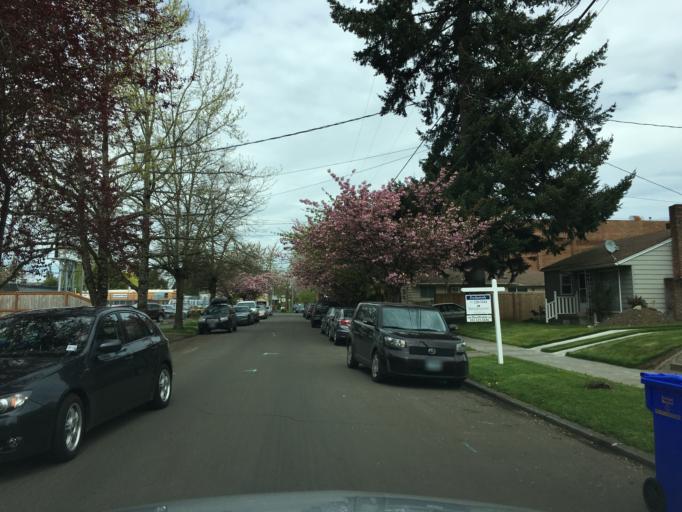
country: US
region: Oregon
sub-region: Multnomah County
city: Lents
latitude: 45.5255
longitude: -122.5847
